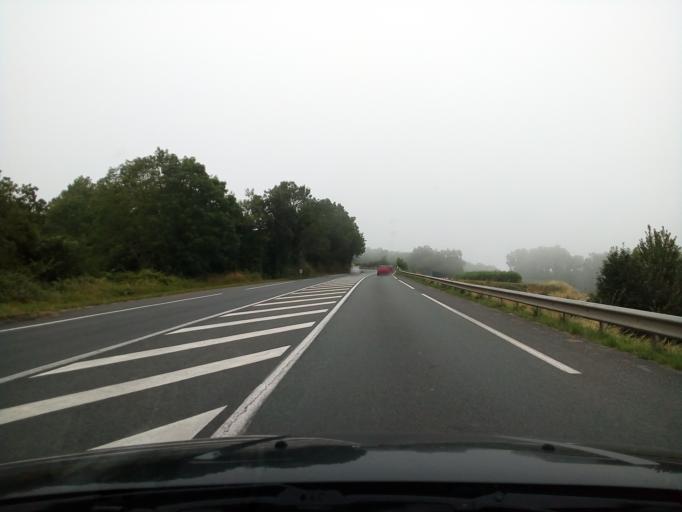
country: FR
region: Poitou-Charentes
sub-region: Departement de la Charente-Maritime
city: Cherac
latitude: 45.6894
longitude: -0.4007
